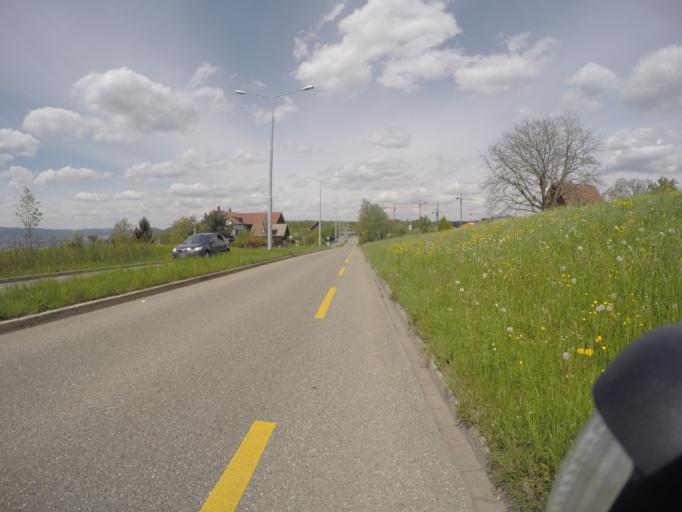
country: CH
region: Zurich
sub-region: Bezirk Zuerich
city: Zuerich (Kreis 10)
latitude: 47.4030
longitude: 8.5072
